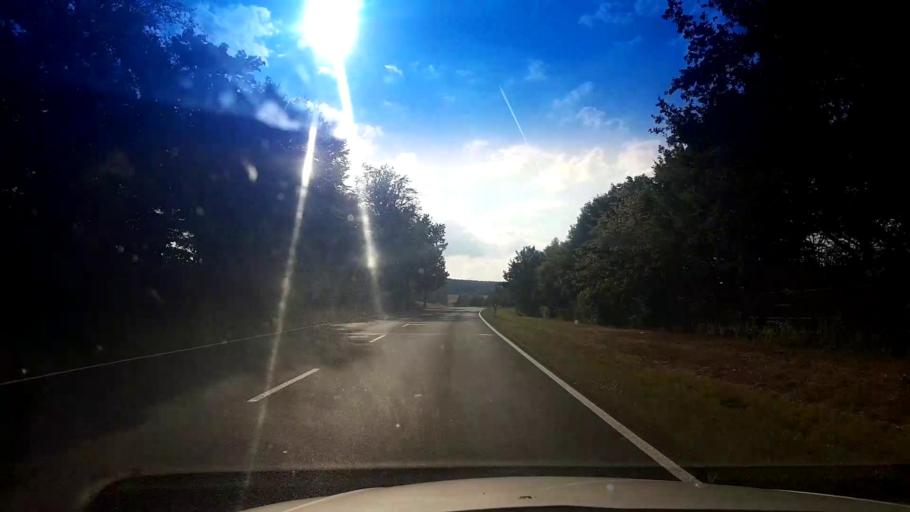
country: DE
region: Bavaria
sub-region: Upper Palatinate
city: Erbendorf
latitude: 49.8330
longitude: 12.0401
